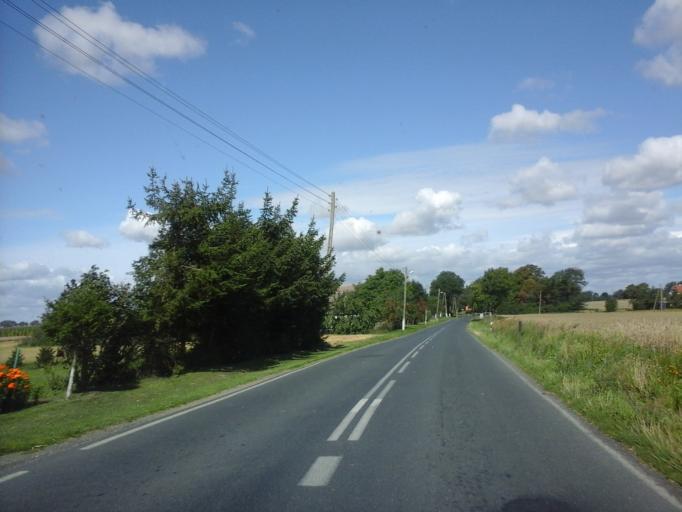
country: PL
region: West Pomeranian Voivodeship
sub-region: Powiat stargardzki
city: Dolice
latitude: 53.2225
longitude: 15.1339
